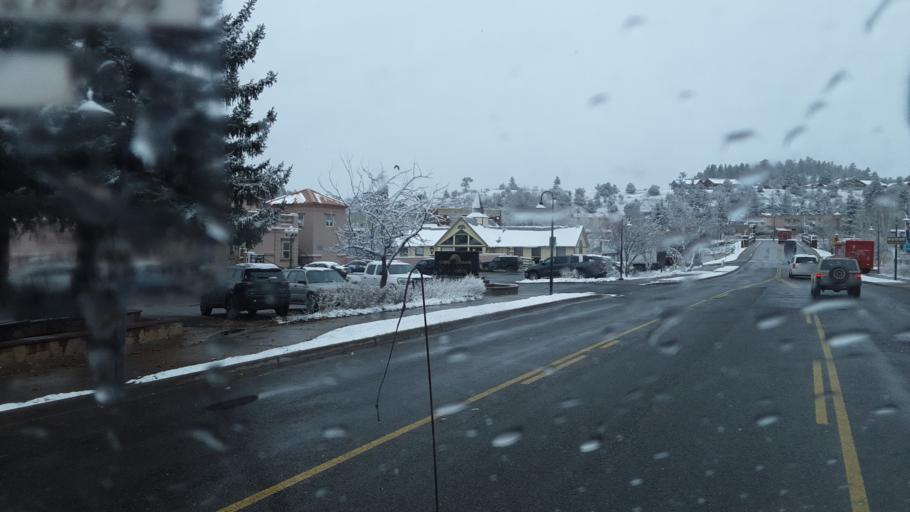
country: US
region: Colorado
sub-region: Archuleta County
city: Pagosa Springs
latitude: 37.2654
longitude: -107.0096
